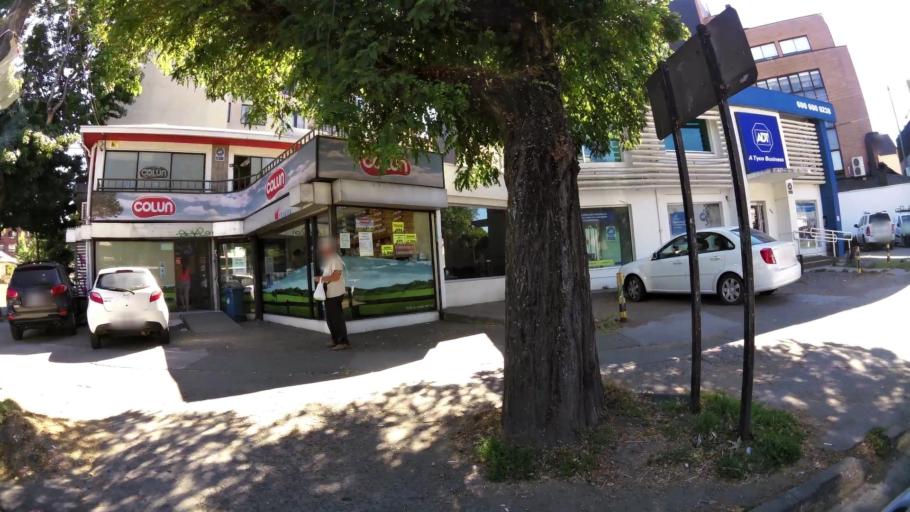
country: CL
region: Biobio
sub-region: Provincia de Concepcion
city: Concepcion
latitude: -36.8217
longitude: -73.0361
